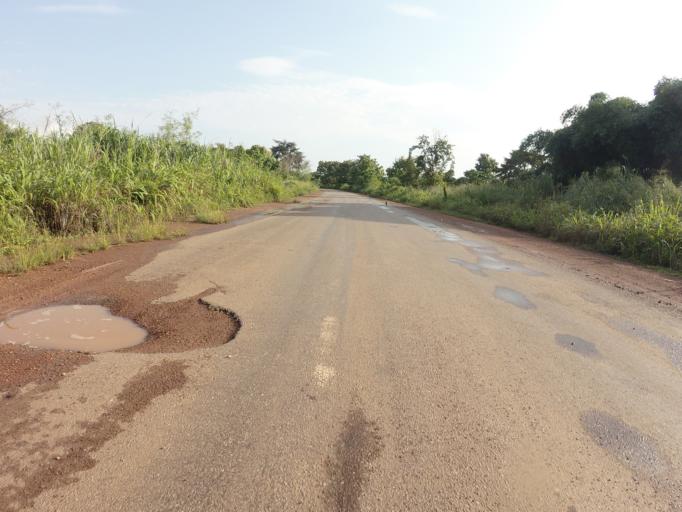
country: GH
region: Volta
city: Hohoe
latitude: 7.0577
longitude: 0.4285
